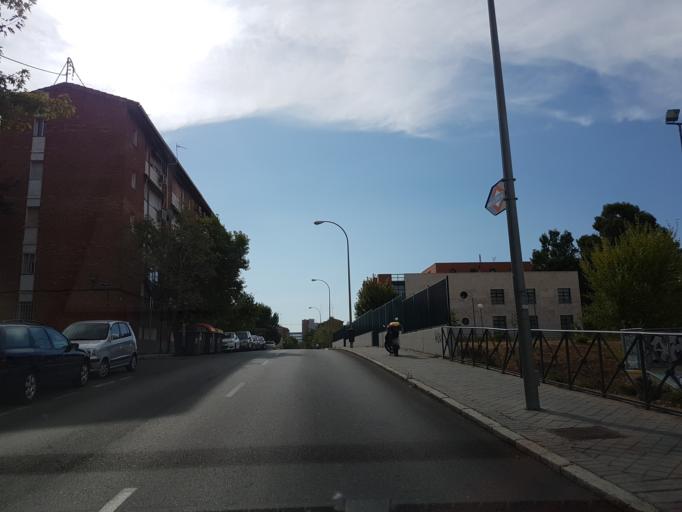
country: ES
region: Madrid
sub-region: Provincia de Madrid
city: Pinar de Chamartin
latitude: 40.4774
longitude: -3.6637
